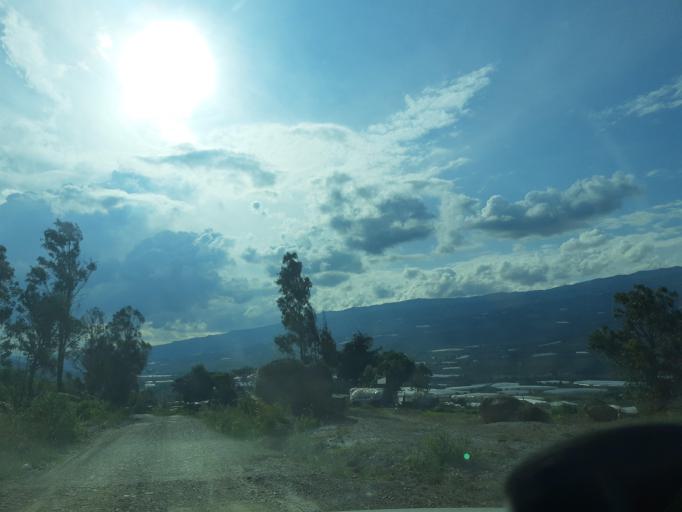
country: CO
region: Boyaca
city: Villa de Leiva
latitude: 5.6668
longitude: -73.5659
